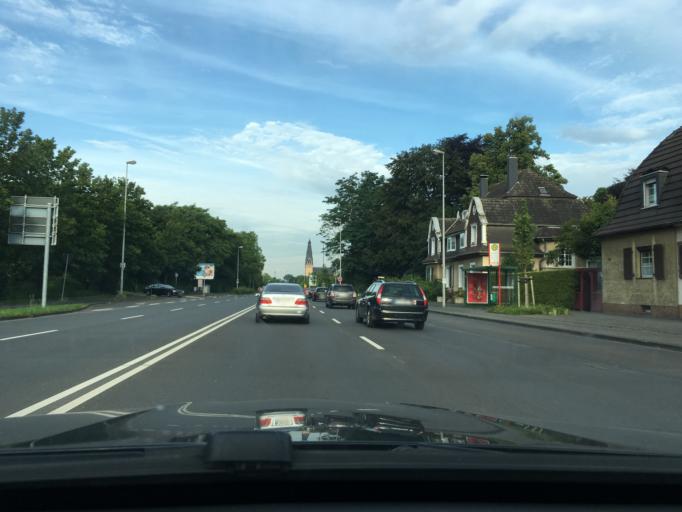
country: DE
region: North Rhine-Westphalia
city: Opladen
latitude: 51.0337
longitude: 7.0211
